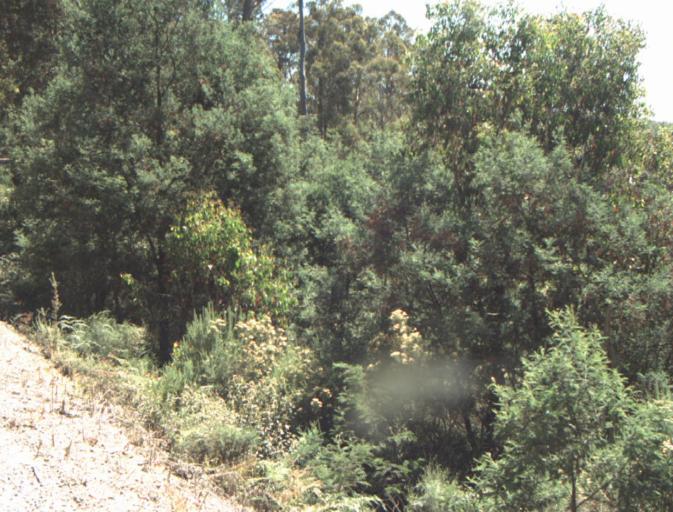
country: AU
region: Tasmania
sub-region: Dorset
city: Scottsdale
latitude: -41.3181
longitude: 147.4627
